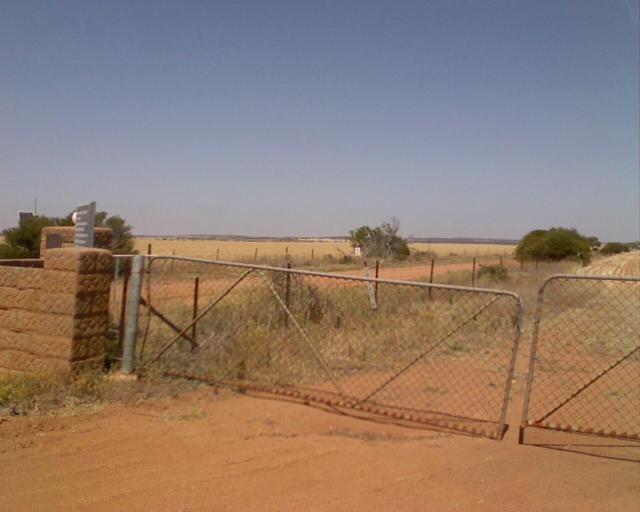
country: AU
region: Western Australia
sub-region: Merredin
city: Merredin
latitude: -30.8317
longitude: 118.2093
